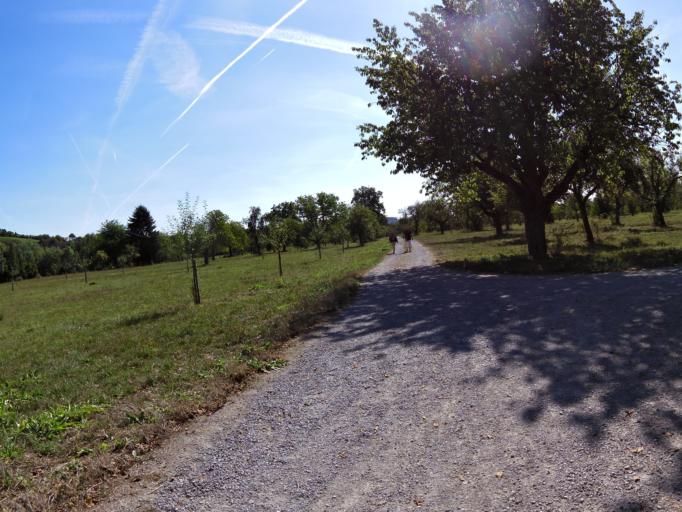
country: DE
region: Bavaria
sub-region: Regierungsbezirk Unterfranken
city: Margetshochheim
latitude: 49.8458
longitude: 9.8624
